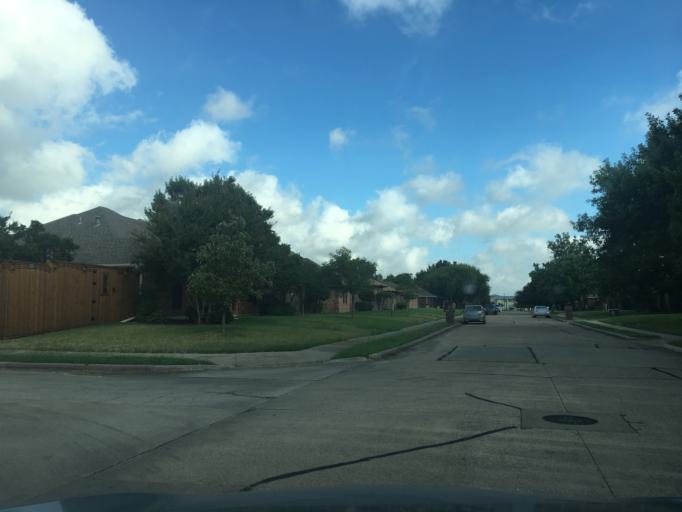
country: US
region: Texas
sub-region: Dallas County
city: Sachse
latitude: 32.9701
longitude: -96.5849
